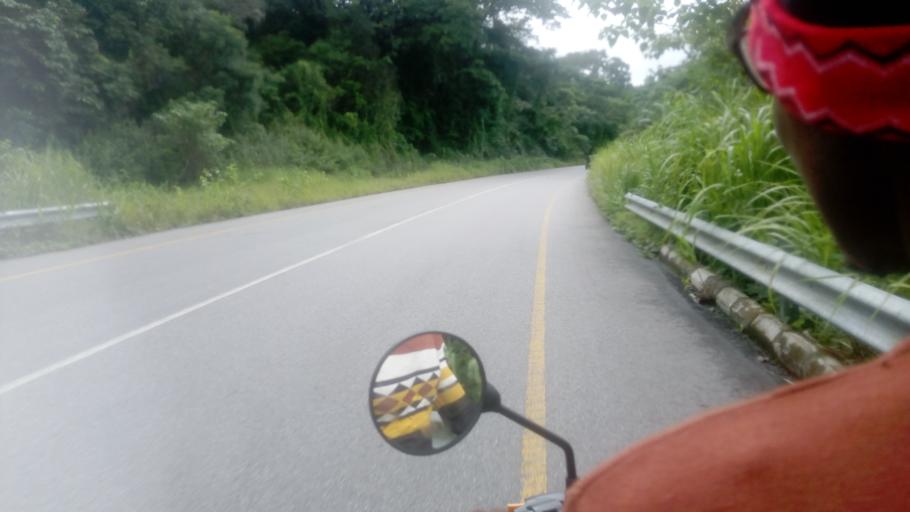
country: SL
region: Northern Province
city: Makali
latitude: 8.6344
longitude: -11.6728
